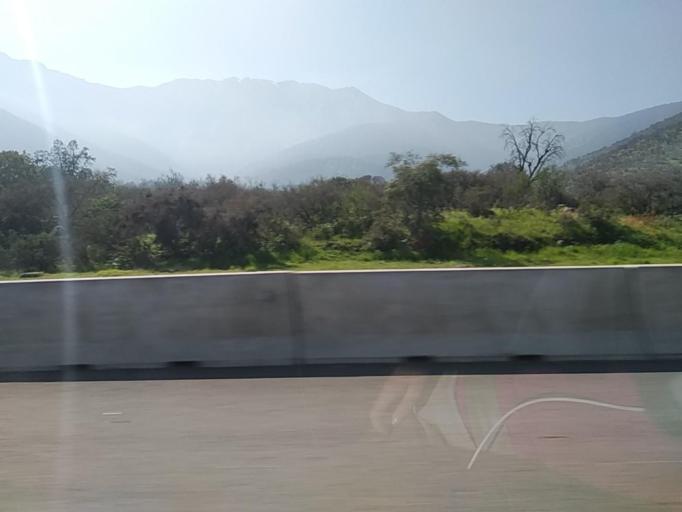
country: CL
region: Santiago Metropolitan
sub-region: Provincia de Chacabuco
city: Lampa
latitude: -33.4435
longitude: -70.9824
